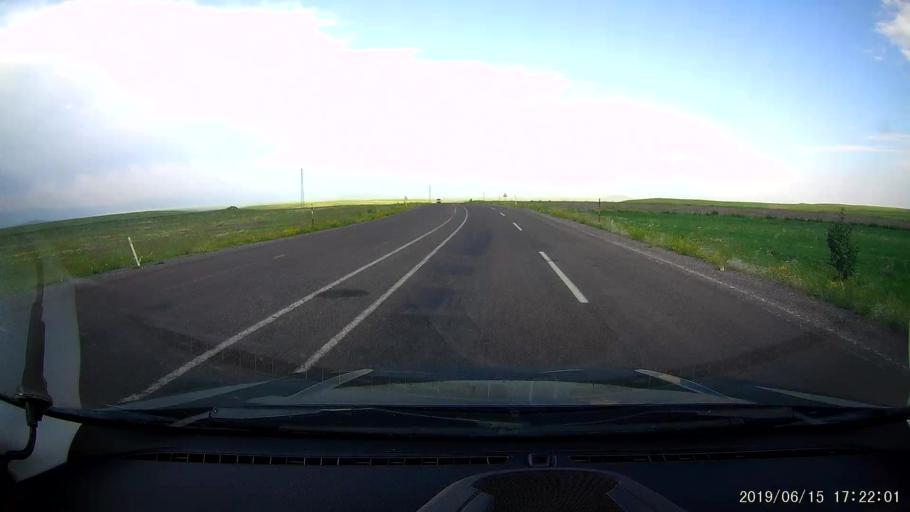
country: TR
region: Kars
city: Basgedikler
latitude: 40.6178
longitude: 43.3353
